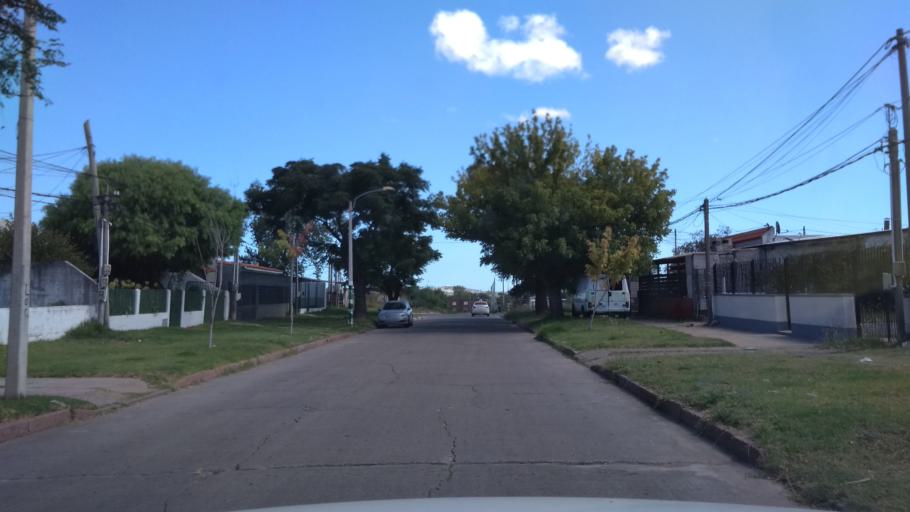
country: UY
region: Canelones
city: La Paz
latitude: -34.8288
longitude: -56.2263
